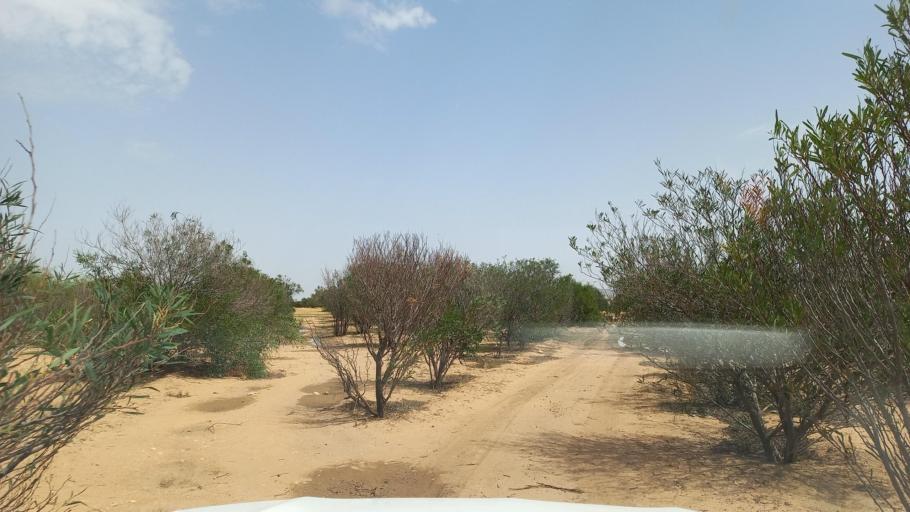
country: TN
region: Al Qasrayn
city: Kasserine
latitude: 35.2938
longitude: 9.0175
